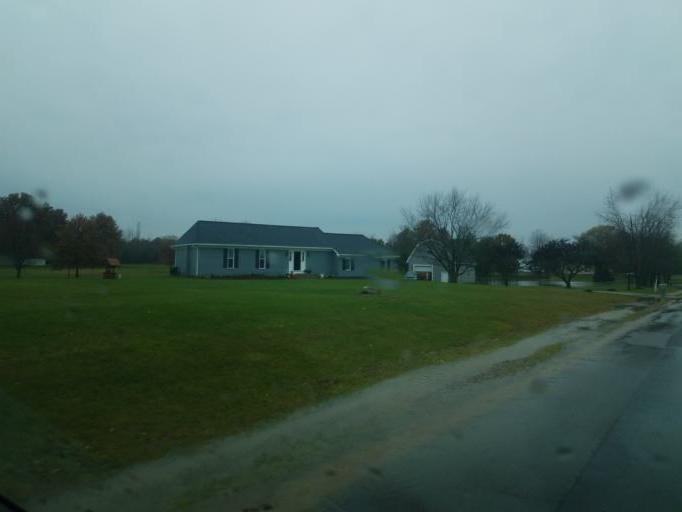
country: US
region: Ohio
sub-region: Knox County
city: Centerburg
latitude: 40.2930
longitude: -82.7386
